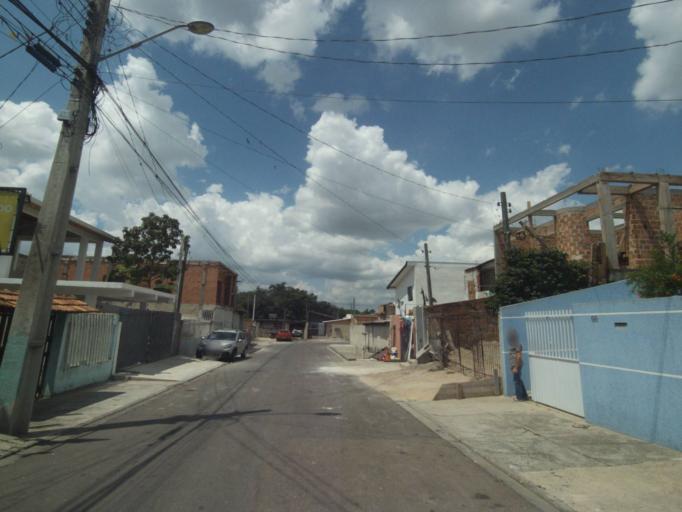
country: BR
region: Parana
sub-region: Sao Jose Dos Pinhais
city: Sao Jose dos Pinhais
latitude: -25.5307
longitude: -49.2751
